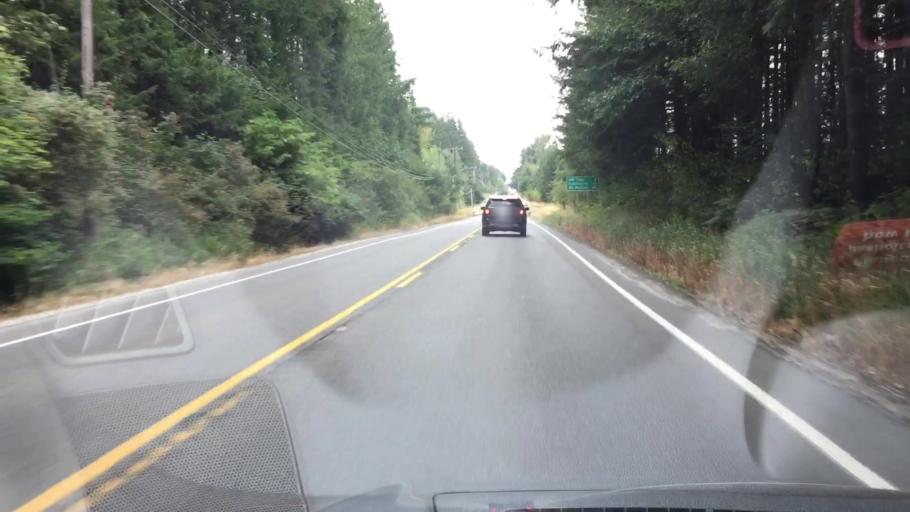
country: US
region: Washington
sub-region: Pierce County
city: Graham
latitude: 46.9772
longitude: -122.2979
